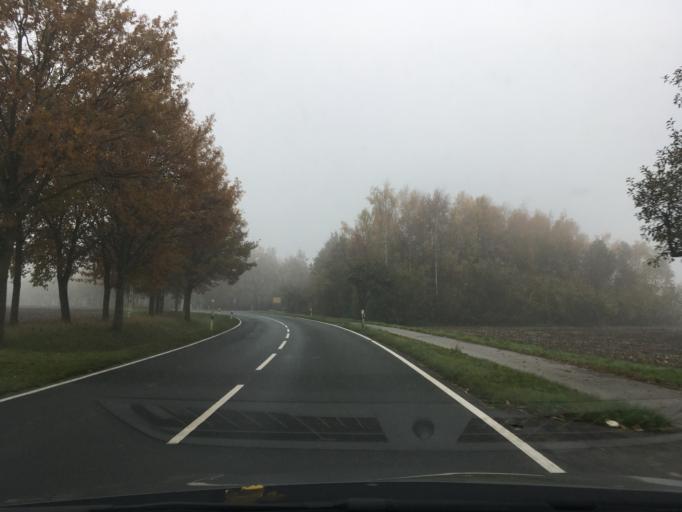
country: DE
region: North Rhine-Westphalia
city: Stadtlohn
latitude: 52.0662
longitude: 6.9278
